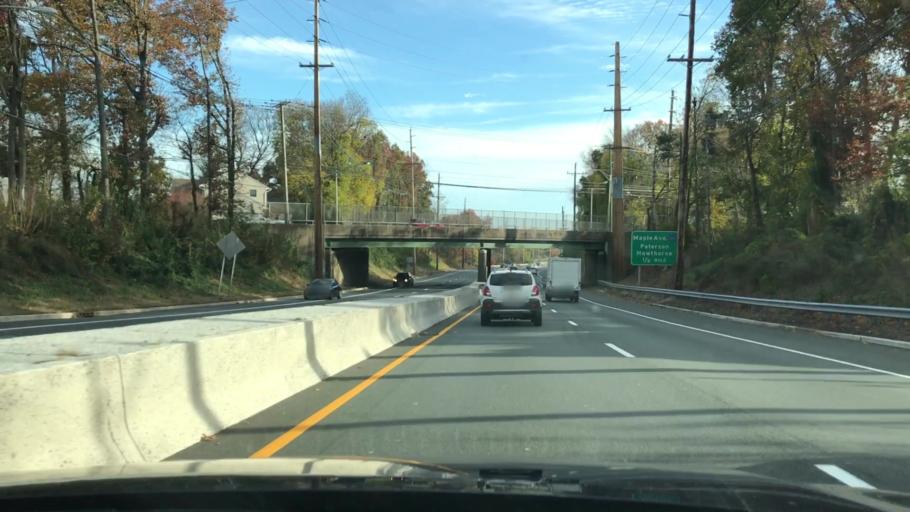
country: US
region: New Jersey
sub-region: Bergen County
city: Glen Rock
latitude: 40.9592
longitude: -74.1442
